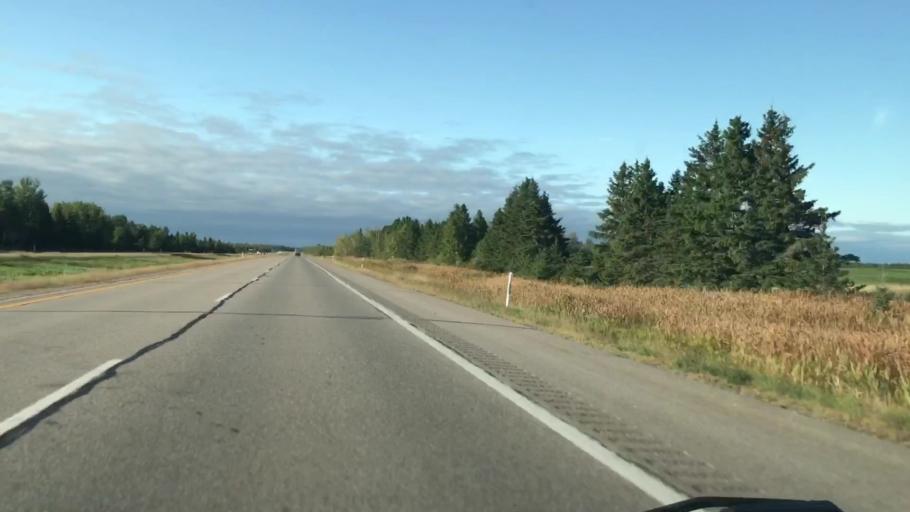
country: US
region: Michigan
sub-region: Chippewa County
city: Sault Ste. Marie
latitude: 46.4165
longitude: -84.3966
